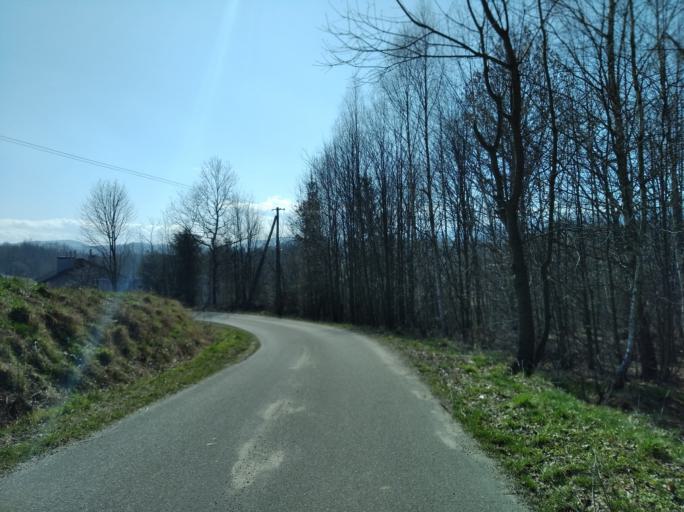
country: PL
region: Subcarpathian Voivodeship
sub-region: Powiat strzyzowski
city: Wysoka Strzyzowska
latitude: 49.8415
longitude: 21.7393
